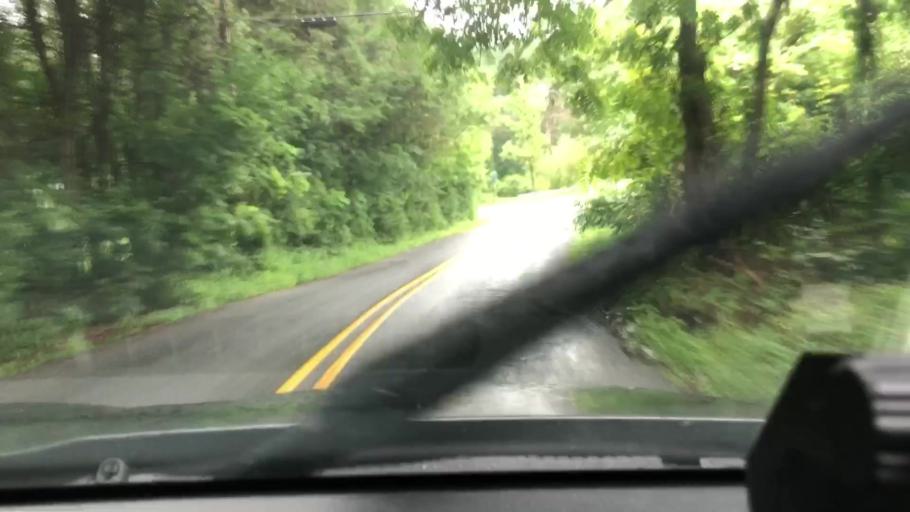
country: US
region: Pennsylvania
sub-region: Lehigh County
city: Macungie
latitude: 40.4836
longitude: -75.5531
